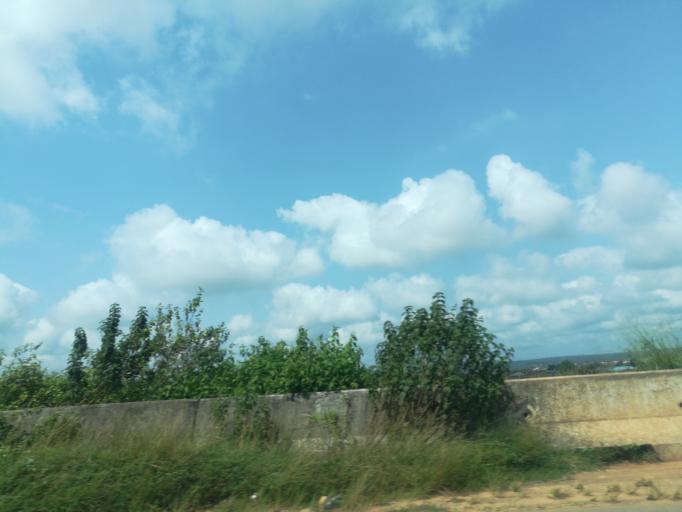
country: NG
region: Oyo
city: Moniya
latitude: 7.5303
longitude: 3.9169
